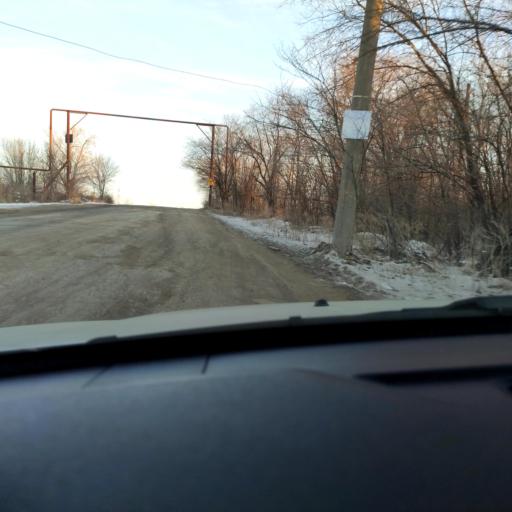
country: RU
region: Samara
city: Smyshlyayevka
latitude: 53.2397
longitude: 50.4807
